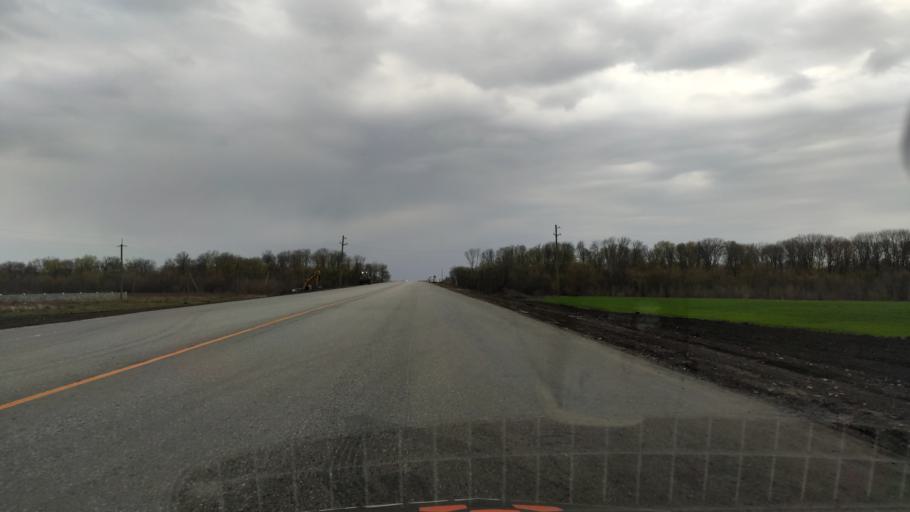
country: RU
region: Kursk
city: Gorshechnoye
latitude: 51.5501
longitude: 38.0452
